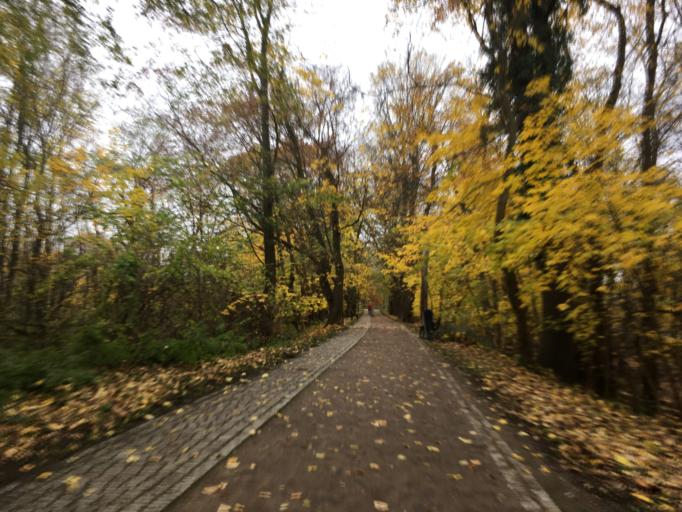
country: PL
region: Lubusz
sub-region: Powiat slubicki
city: Slubice
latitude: 52.3399
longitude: 14.5594
